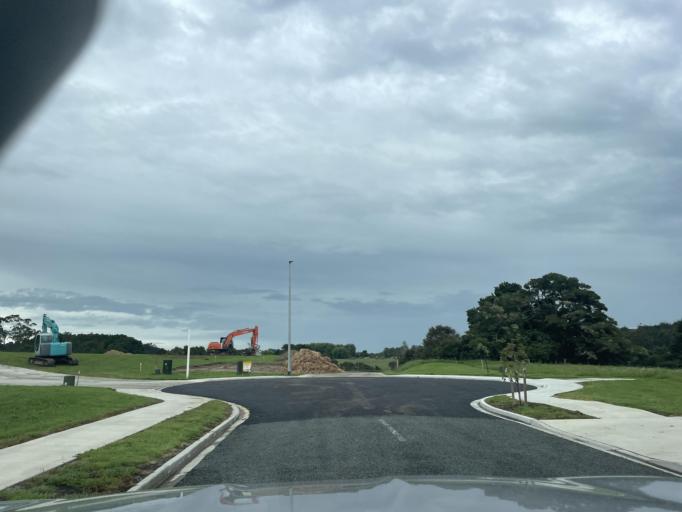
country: NZ
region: Northland
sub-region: Whangarei
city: Ruakaka
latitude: -36.0990
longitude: 174.2306
